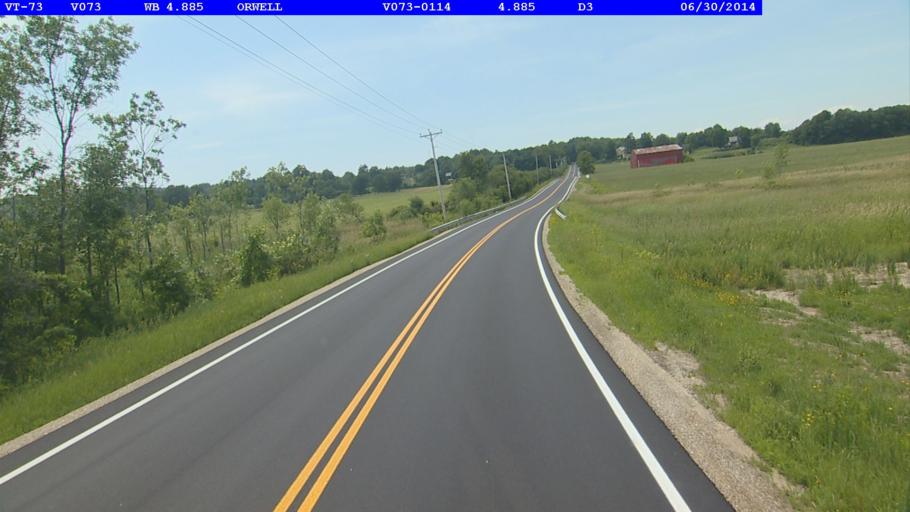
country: US
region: Vermont
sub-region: Rutland County
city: Brandon
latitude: 43.7949
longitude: -73.2133
